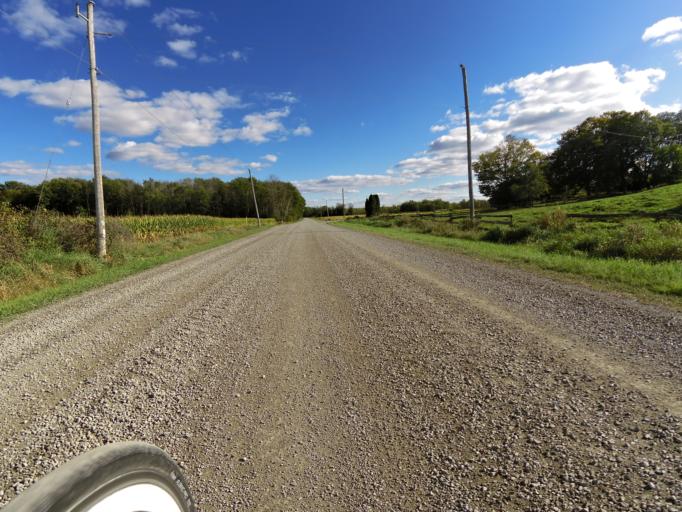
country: CA
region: Ontario
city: Bells Corners
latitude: 45.1407
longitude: -75.6589
